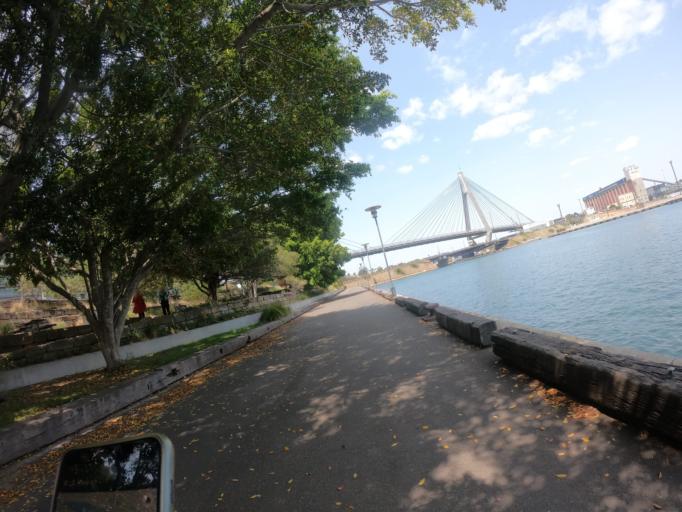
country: AU
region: New South Wales
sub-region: Leichhardt
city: Balmain East
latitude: -33.8672
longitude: 151.1884
